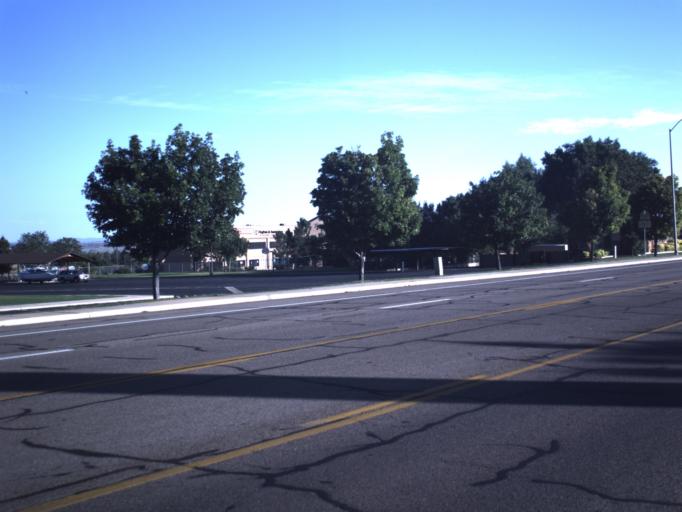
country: US
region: Utah
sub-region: Iron County
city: Cedar City
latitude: 37.7133
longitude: -113.0606
